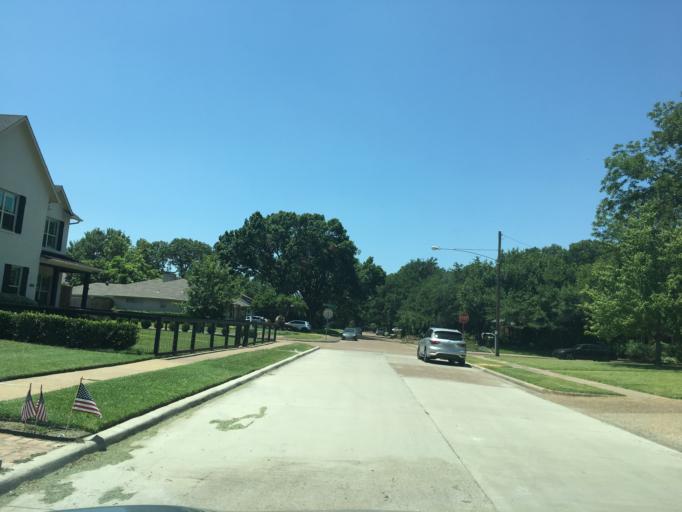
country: US
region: Texas
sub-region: Dallas County
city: Highland Park
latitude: 32.8410
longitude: -96.7416
